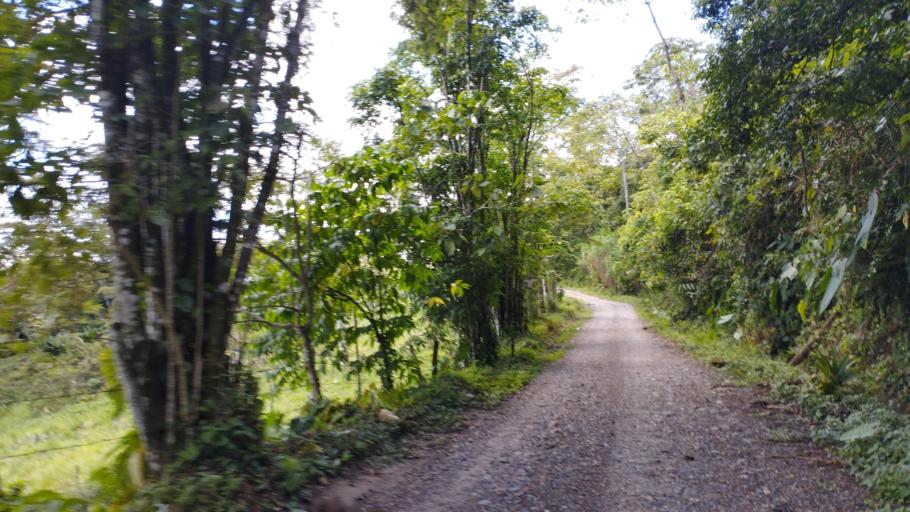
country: CO
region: Boyaca
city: San Luis de Gaceno
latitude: 4.7815
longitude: -73.1219
